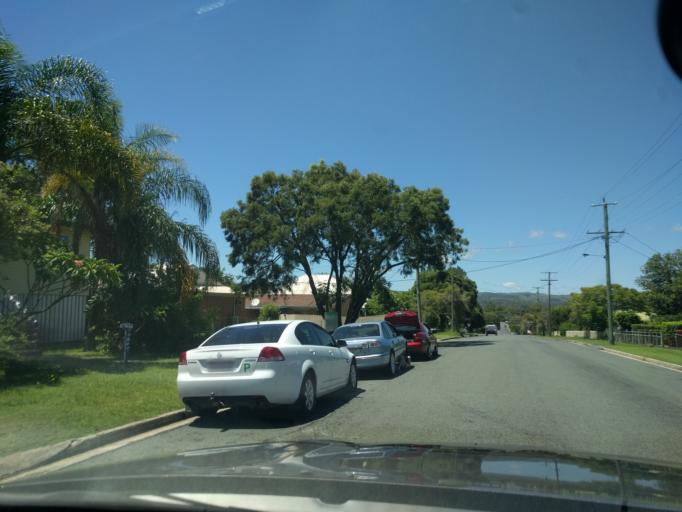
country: AU
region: Queensland
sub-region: Logan
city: Cedar Vale
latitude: -27.9859
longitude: 153.0009
